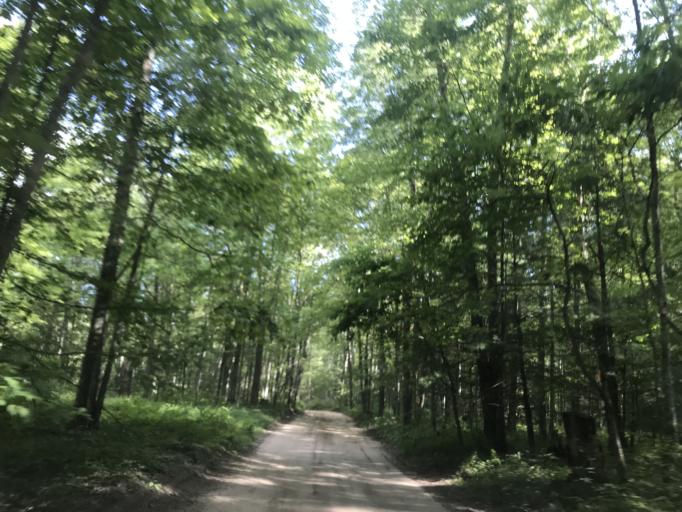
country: US
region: Michigan
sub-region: Newaygo County
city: Newaygo
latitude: 43.4594
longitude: -85.7629
